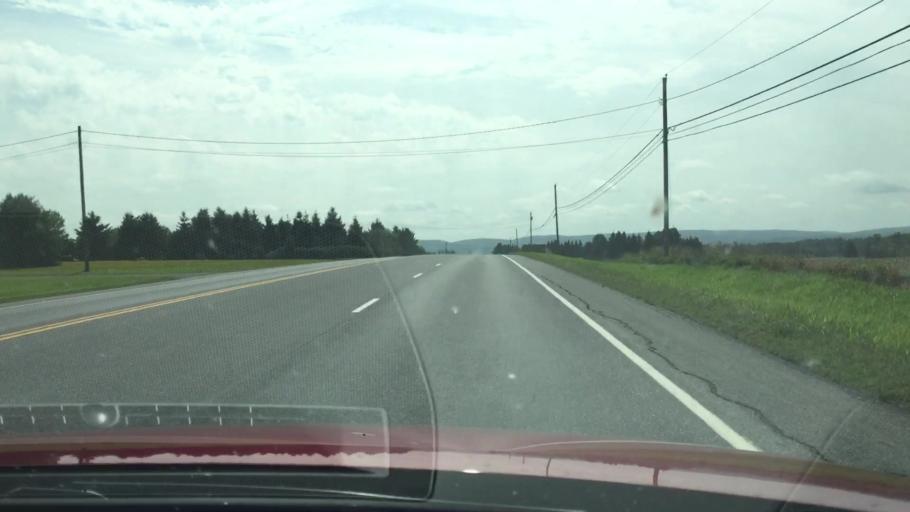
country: US
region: Maine
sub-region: Aroostook County
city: Easton
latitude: 46.5773
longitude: -67.9553
